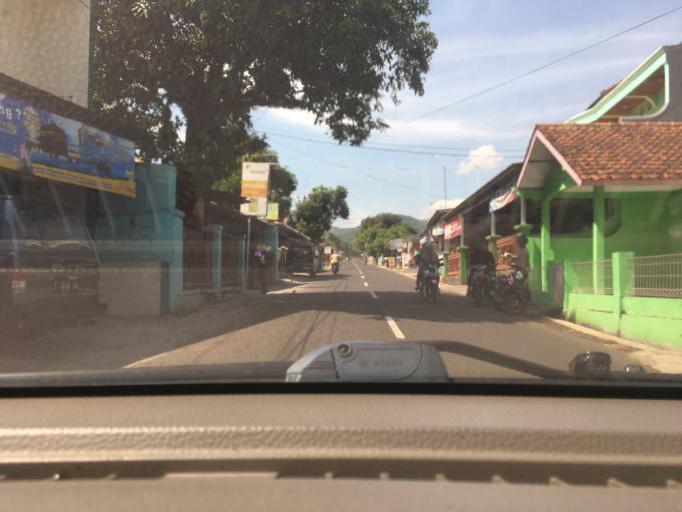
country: ID
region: West Java
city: Cilengkrang
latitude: -6.9494
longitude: 108.0929
